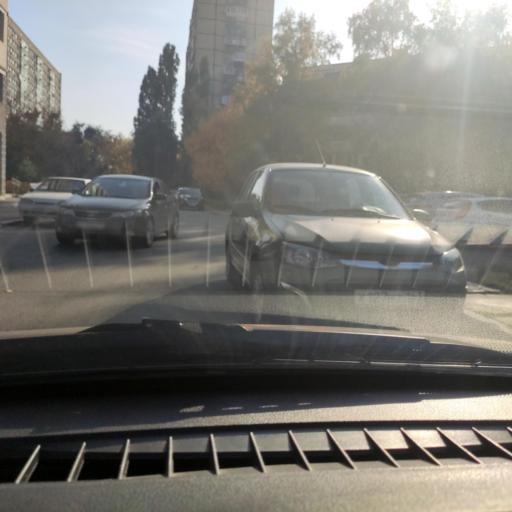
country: RU
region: Samara
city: Tol'yatti
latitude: 53.5184
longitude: 49.2895
